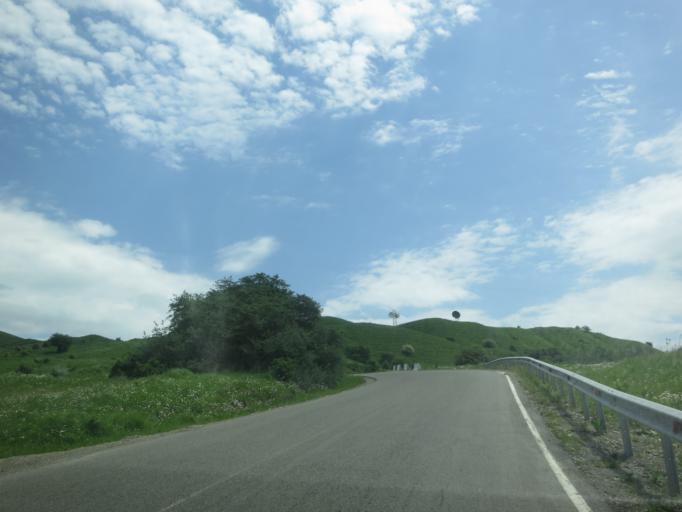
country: GE
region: Kakheti
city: Sagarejo
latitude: 41.8654
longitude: 45.2755
